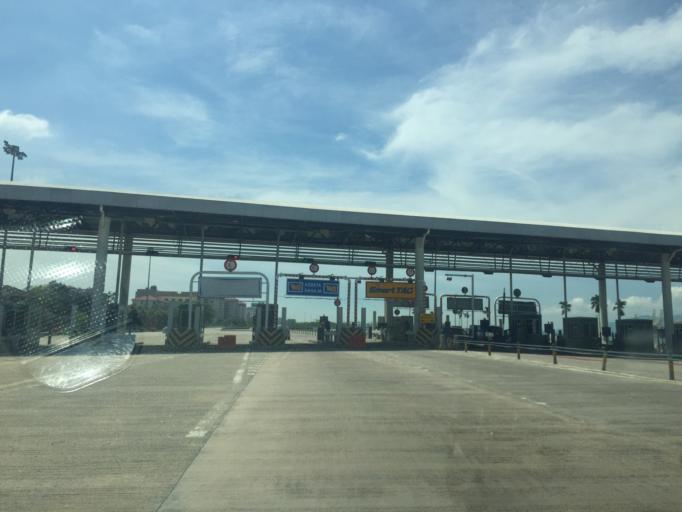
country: MY
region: Penang
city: Permatang Kuching
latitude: 5.4319
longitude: 100.3770
